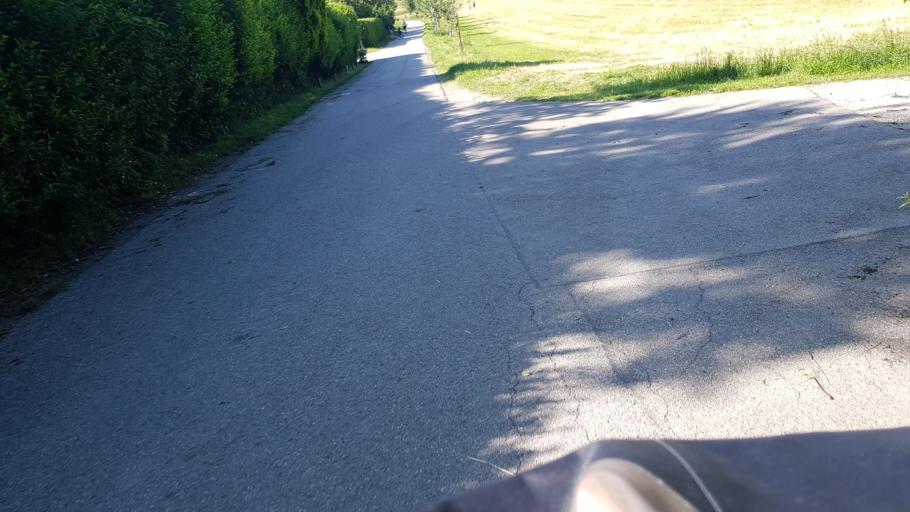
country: DE
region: Bavaria
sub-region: Upper Bavaria
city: Starnberg
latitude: 48.0249
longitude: 11.3717
